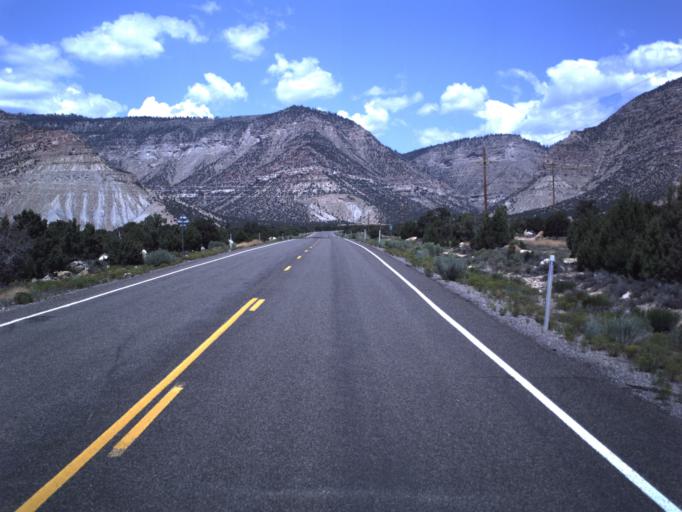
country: US
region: Utah
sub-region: Emery County
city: Orangeville
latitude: 39.2851
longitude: -111.1061
